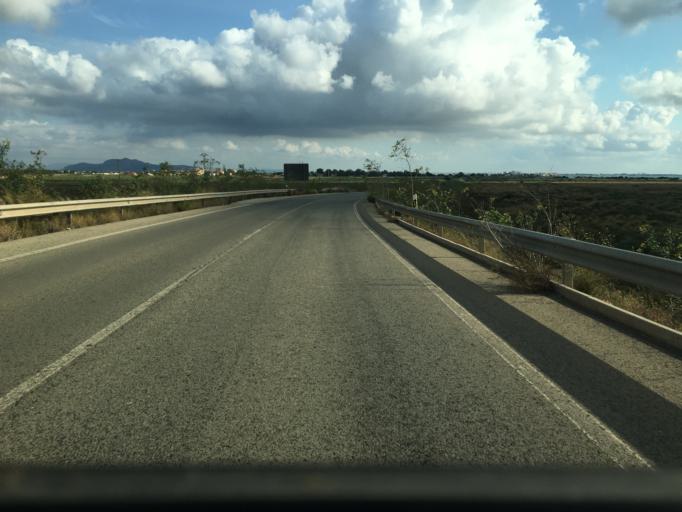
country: ES
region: Murcia
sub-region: Murcia
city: Los Alcazares
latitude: 37.7063
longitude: -0.8634
